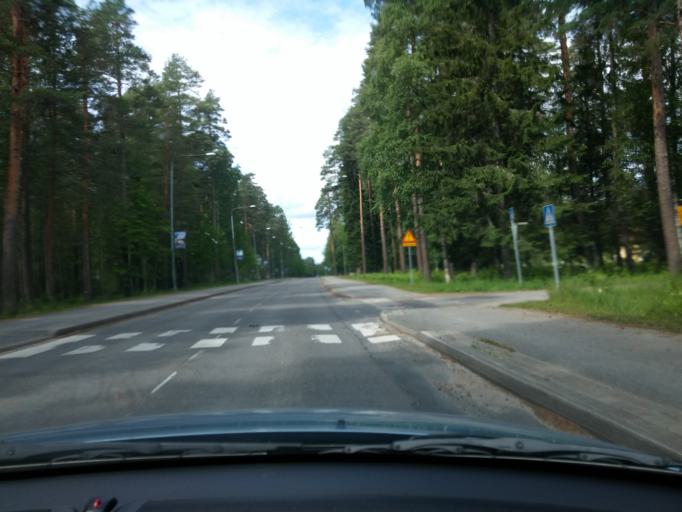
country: FI
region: Central Finland
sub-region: Saarijaervi-Viitasaari
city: Saarijaervi
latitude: 62.7058
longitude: 25.2349
